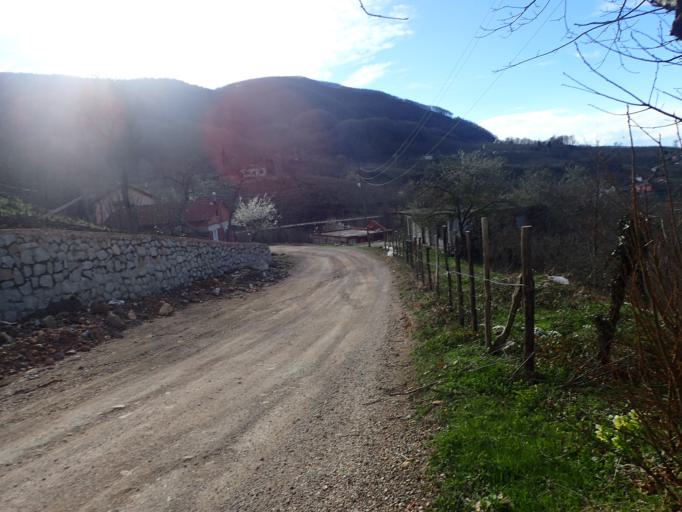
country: TR
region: Ordu
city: Kumru
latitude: 40.9290
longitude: 37.2464
